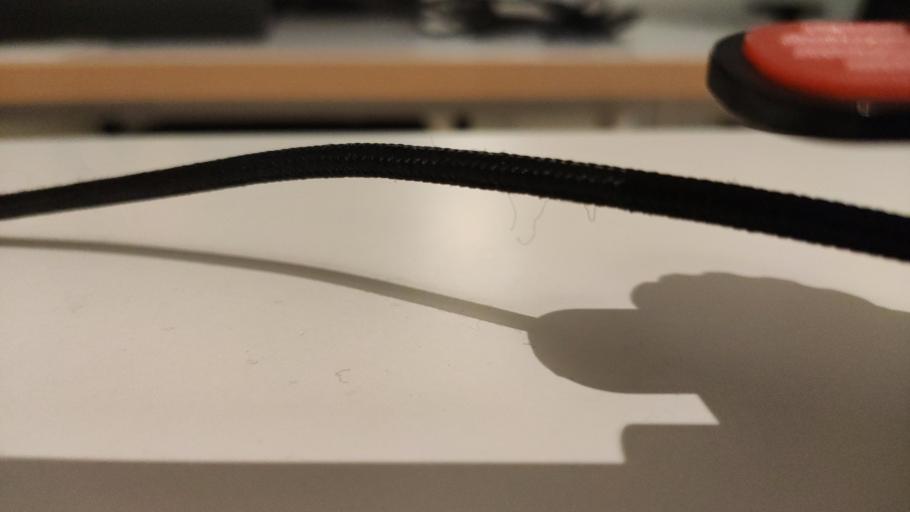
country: RU
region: Moskovskaya
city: Novosin'kovo
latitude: 56.3975
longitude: 37.2679
